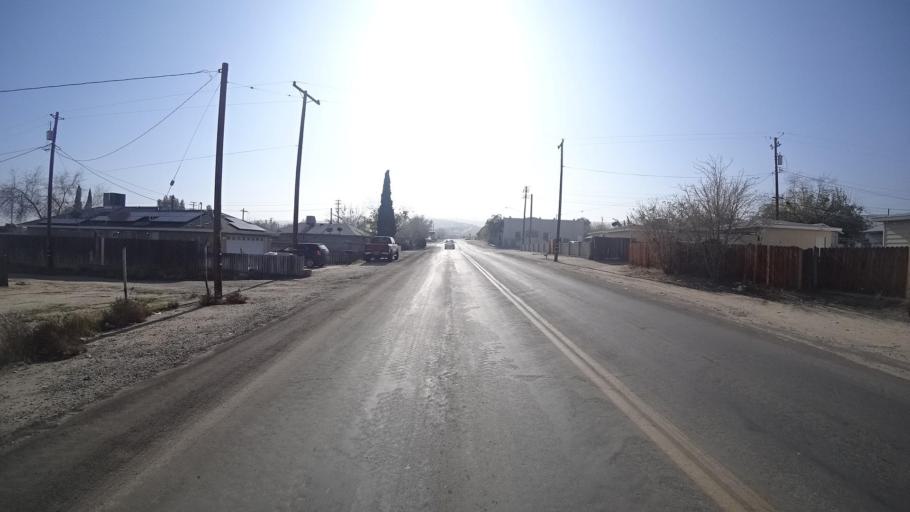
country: US
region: California
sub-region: Kern County
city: Taft Heights
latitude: 35.1340
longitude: -119.4650
